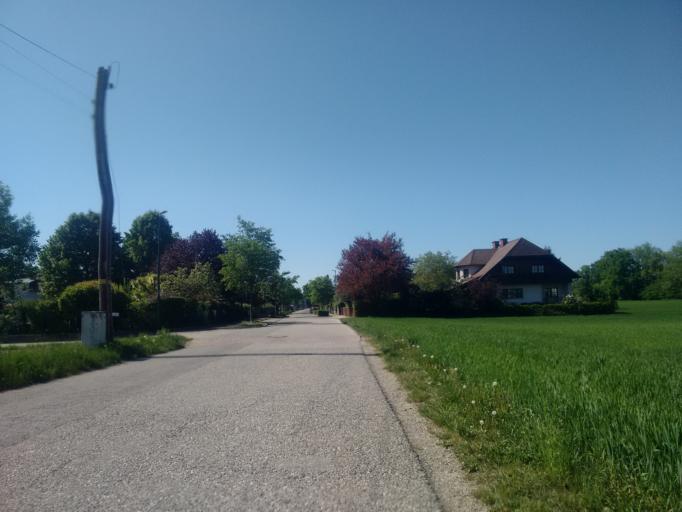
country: AT
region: Upper Austria
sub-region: Wels Stadt
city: Wels
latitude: 48.1682
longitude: 14.0015
